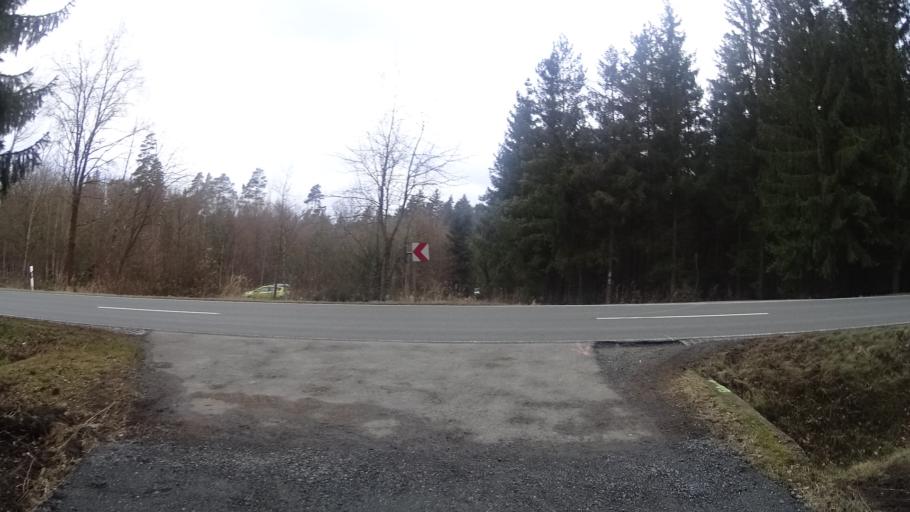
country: DE
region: Saxony
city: Pausa
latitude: 50.6101
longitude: 11.9962
